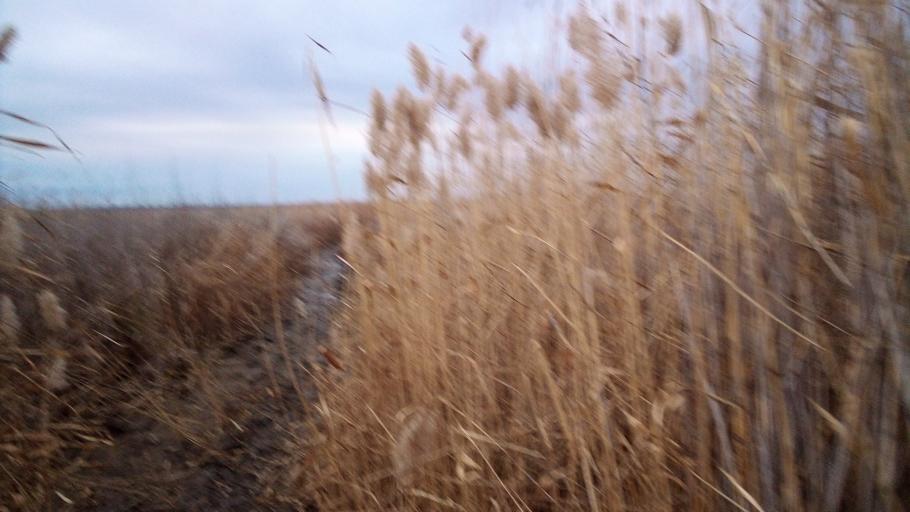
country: RU
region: Chelyabinsk
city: Novosineglazovskiy
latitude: 54.9868
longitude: 61.4029
